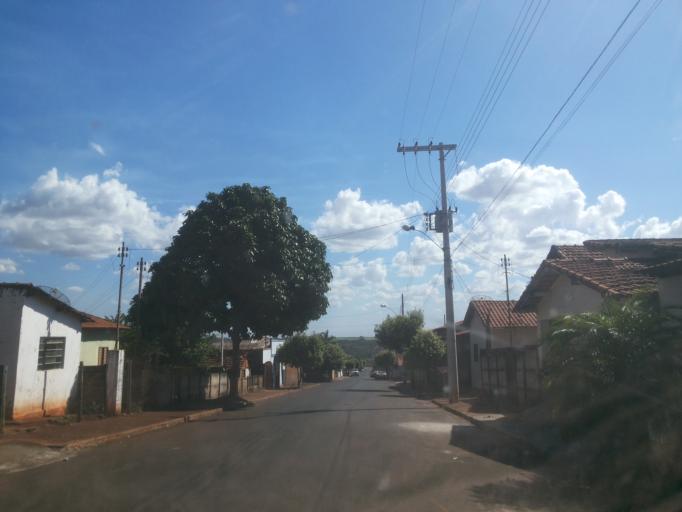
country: BR
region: Minas Gerais
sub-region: Capinopolis
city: Capinopolis
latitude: -18.6867
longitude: -49.5700
